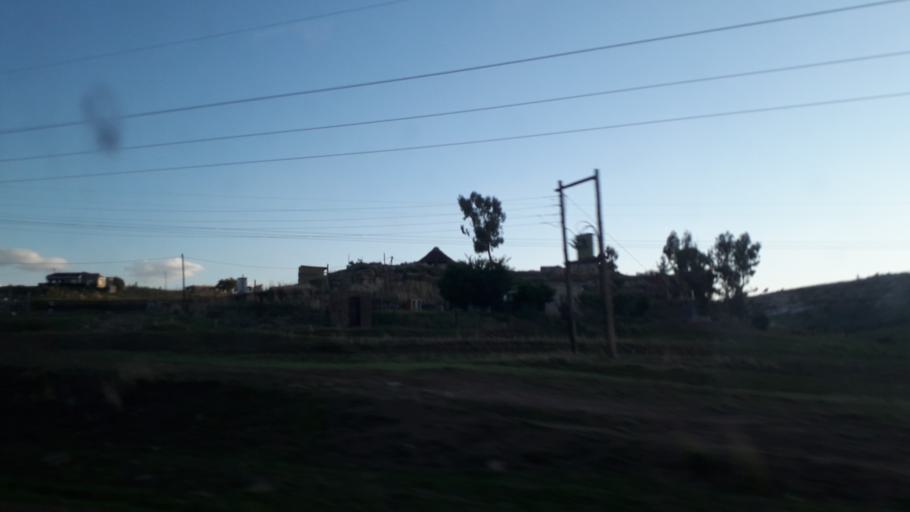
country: LS
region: Butha-Buthe
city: Butha-Buthe
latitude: -28.7328
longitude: 28.4026
